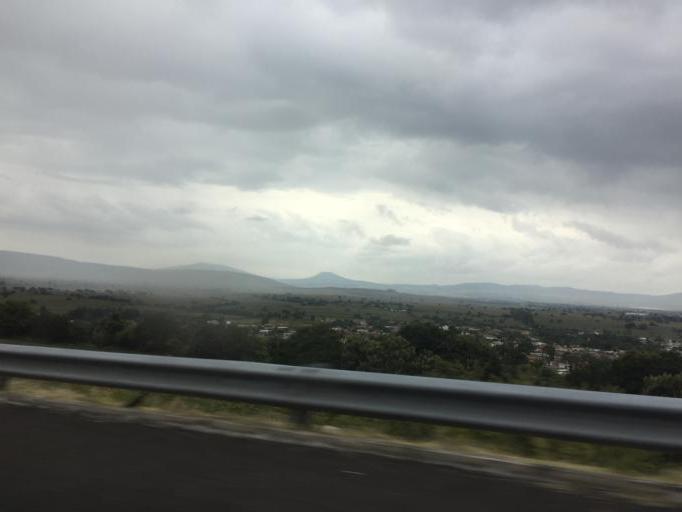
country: MX
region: Jalisco
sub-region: Zapotlan del Rey
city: Zapotlan del Rey
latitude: 20.4728
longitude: -102.9215
